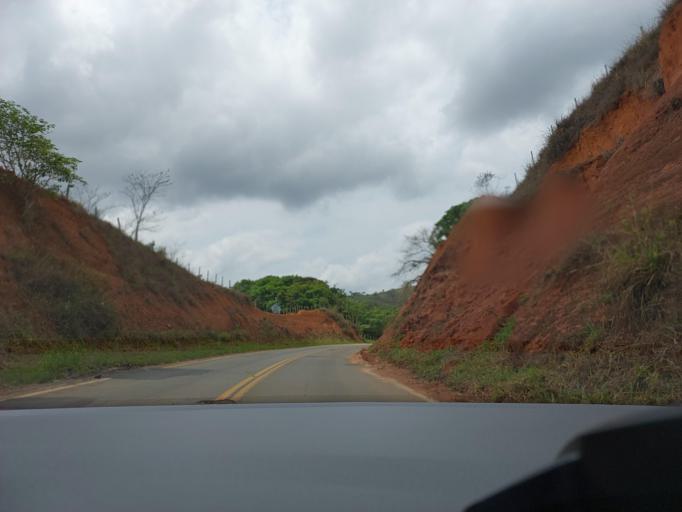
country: BR
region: Minas Gerais
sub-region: Ponte Nova
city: Ponte Nova
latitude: -20.3831
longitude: -42.8844
